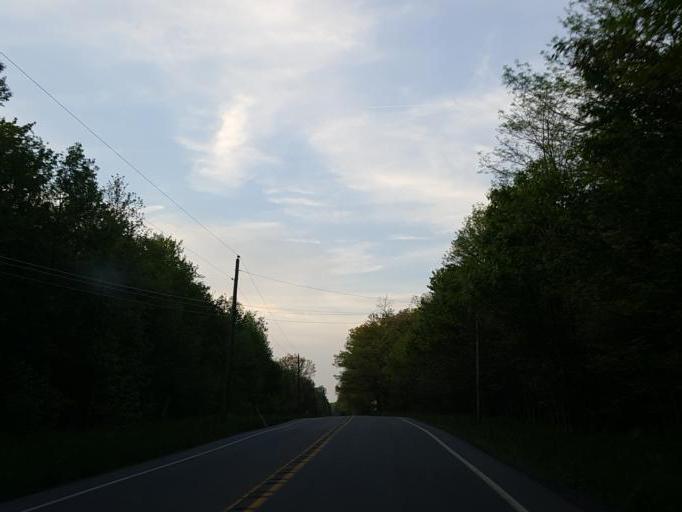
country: US
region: Pennsylvania
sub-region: Cambria County
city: Gallitzin
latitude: 40.4998
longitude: -78.5408
